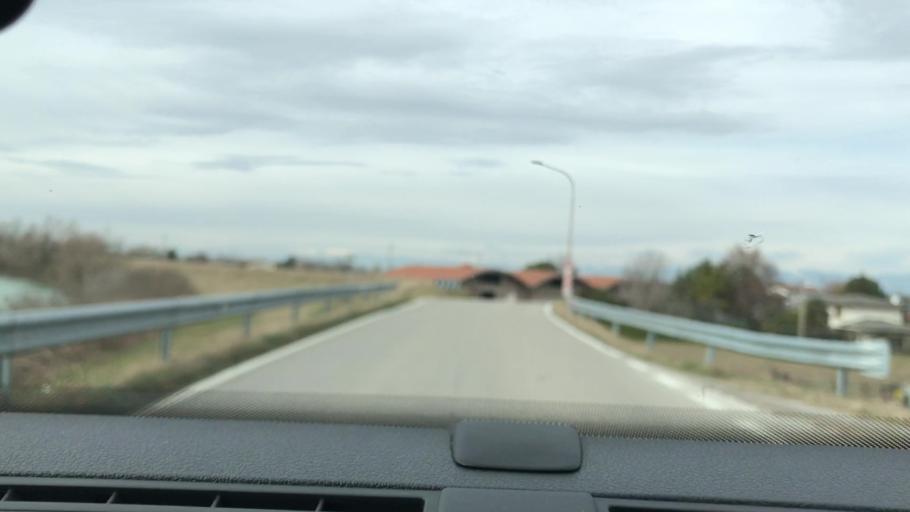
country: IT
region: Veneto
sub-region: Provincia di Venezia
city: Santo Stino di Livenza
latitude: 45.7181
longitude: 12.6831
